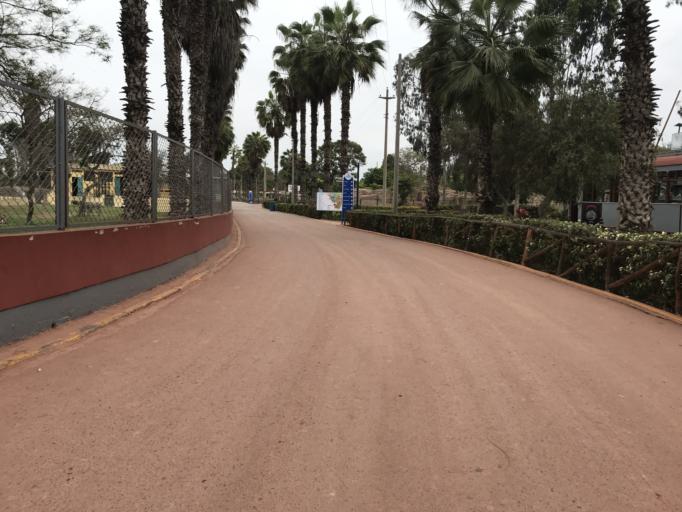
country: PE
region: Callao
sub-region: Callao
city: Callao
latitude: -12.0690
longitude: -77.0841
